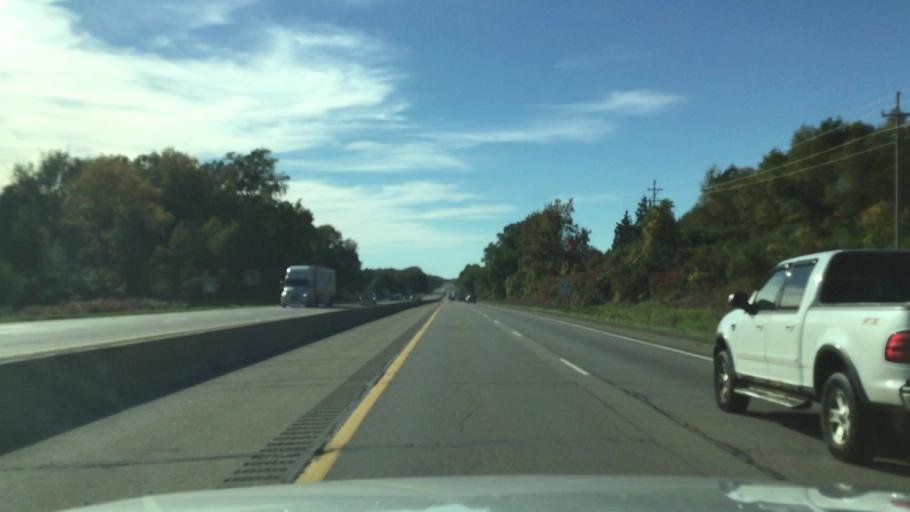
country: US
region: Michigan
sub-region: Jackson County
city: Spring Arbor
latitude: 42.2691
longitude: -84.5535
